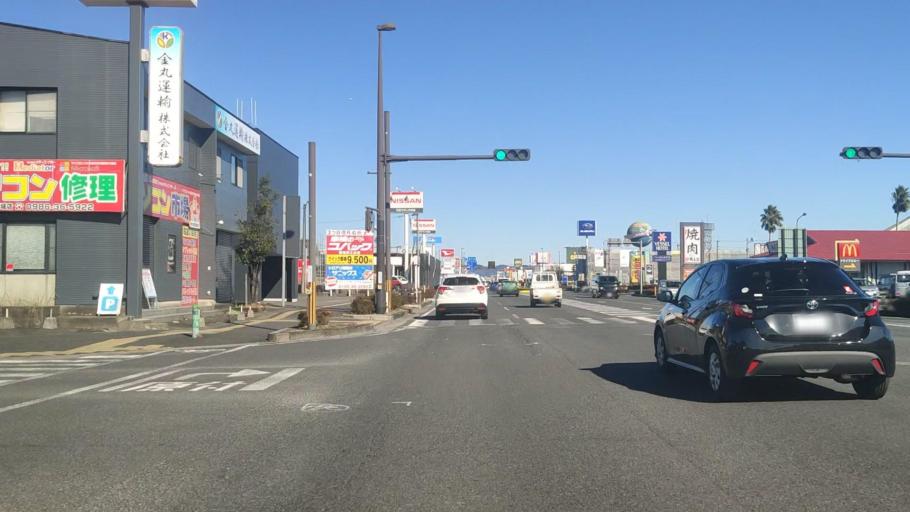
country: JP
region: Miyazaki
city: Miyakonojo
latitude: 31.7583
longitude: 131.0845
